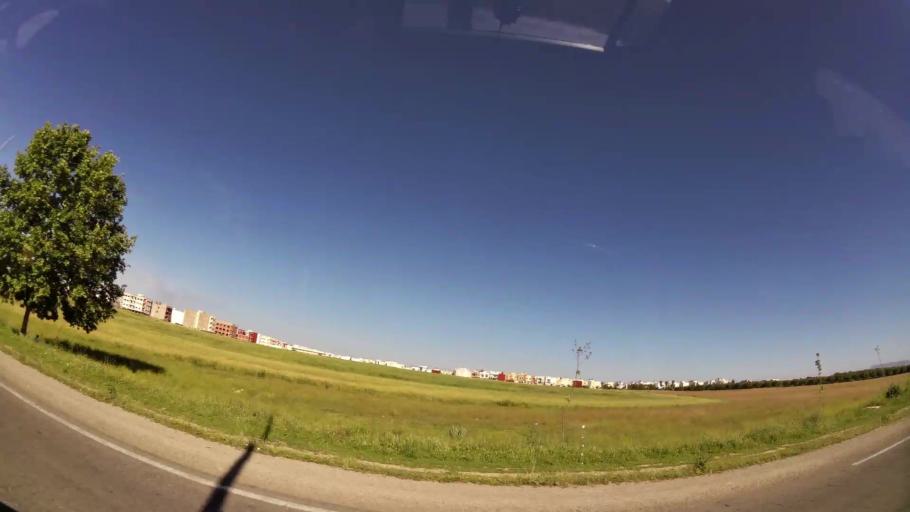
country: MA
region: Fes-Boulemane
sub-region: Fes
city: Fes
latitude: 34.0018
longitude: -5.0235
